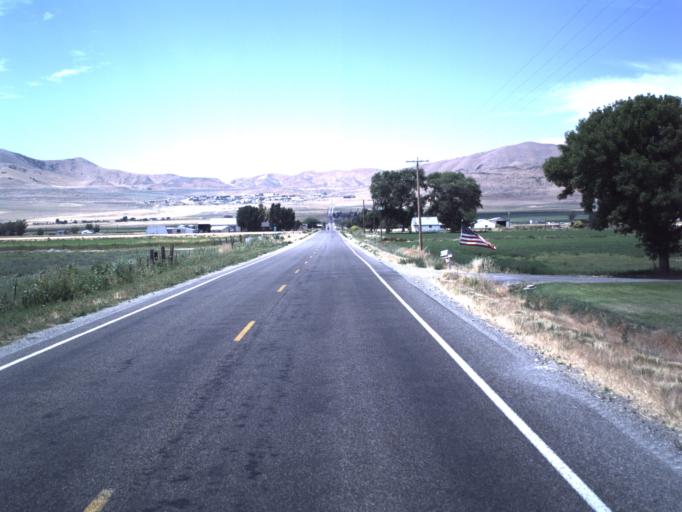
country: US
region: Utah
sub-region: Box Elder County
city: Tremonton
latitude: 41.7096
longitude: -112.2665
